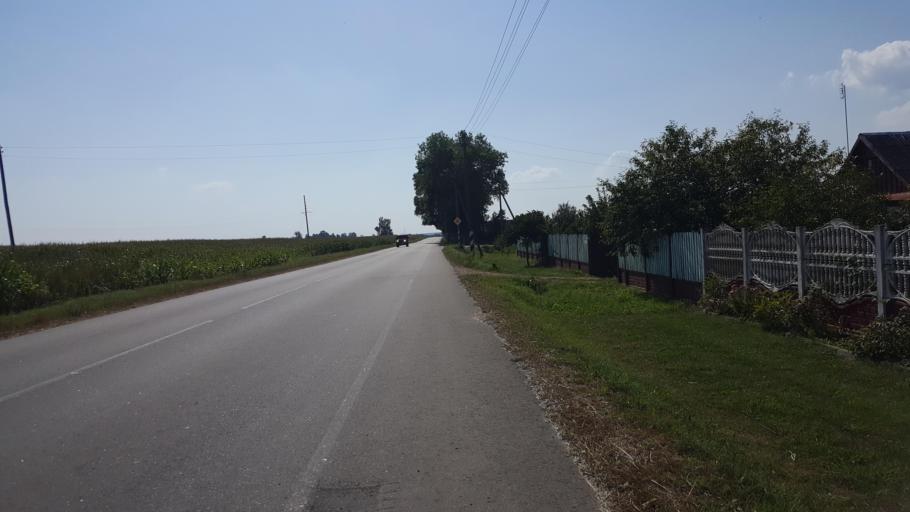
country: PL
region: Podlasie
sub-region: Powiat hajnowski
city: Czeremcha
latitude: 52.4898
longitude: 23.5521
